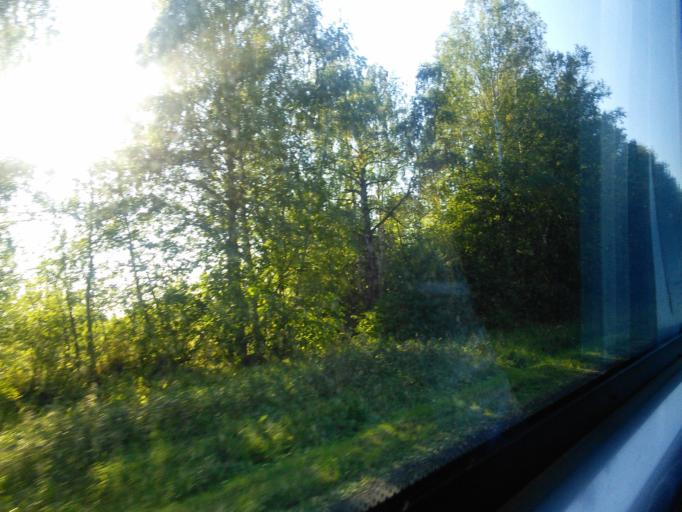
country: RU
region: Jaroslavl
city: Poshekhon'ye
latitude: 58.3654
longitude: 39.0283
